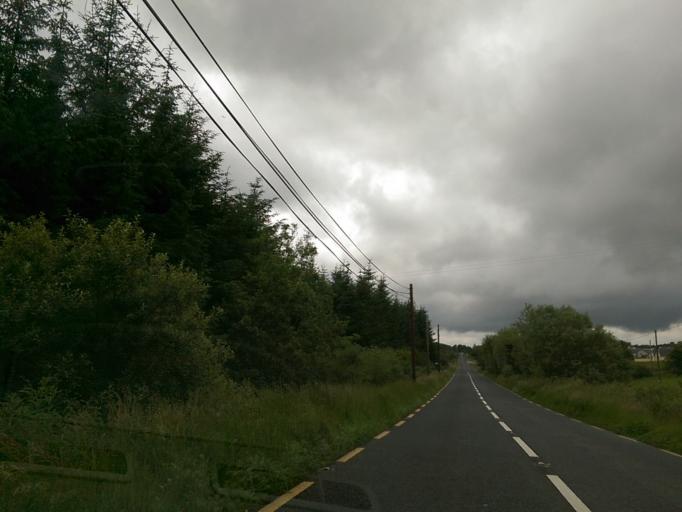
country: IE
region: Munster
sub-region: An Clar
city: Ennis
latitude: 52.7622
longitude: -9.1167
